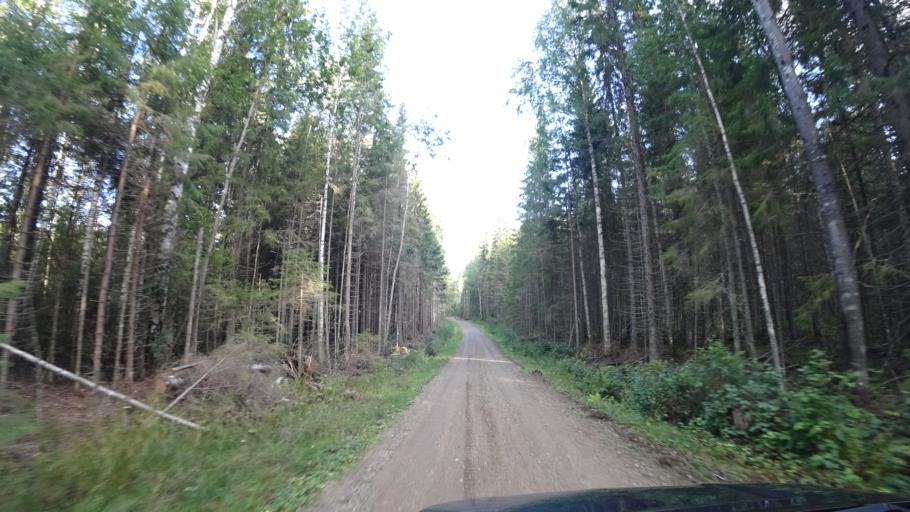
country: FI
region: Paijanne Tavastia
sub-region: Lahti
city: Auttoinen
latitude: 61.2197
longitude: 25.2061
